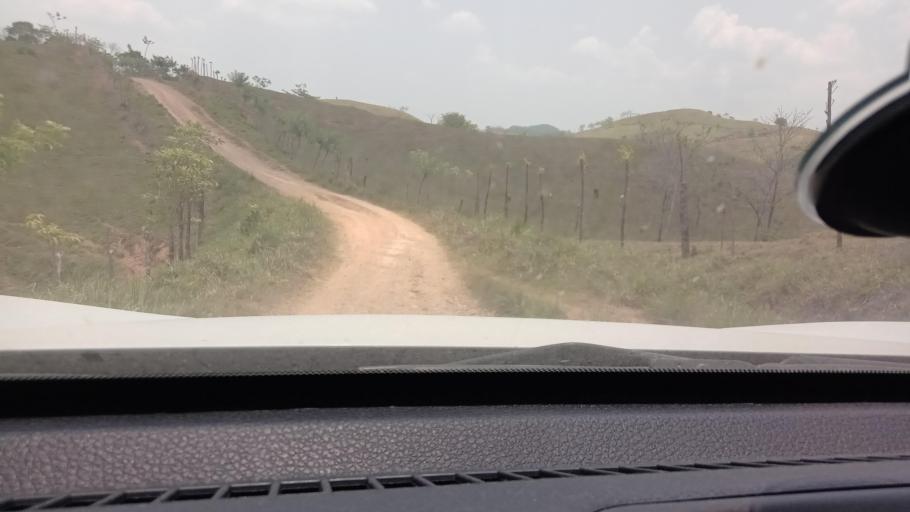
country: MX
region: Tabasco
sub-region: Huimanguillo
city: Francisco Rueda
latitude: 17.4939
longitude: -93.9248
